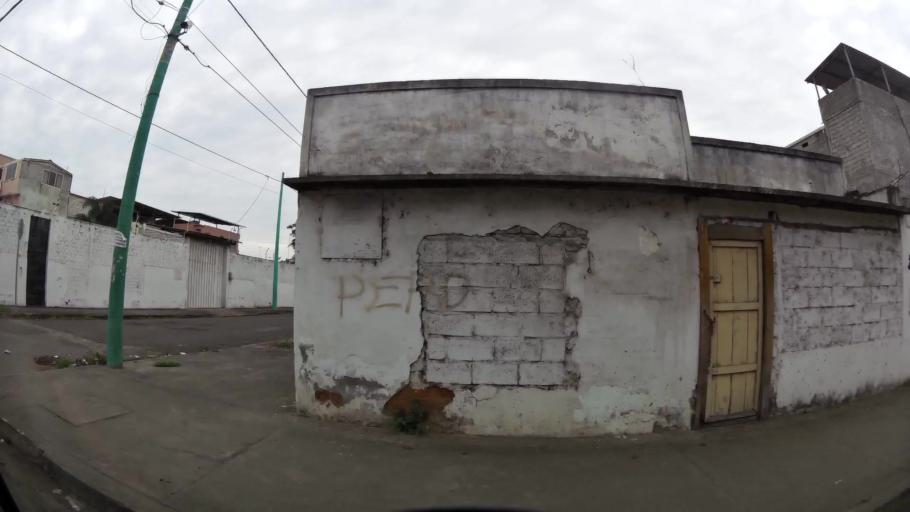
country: EC
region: El Oro
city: Machala
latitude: -3.2593
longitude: -79.9427
